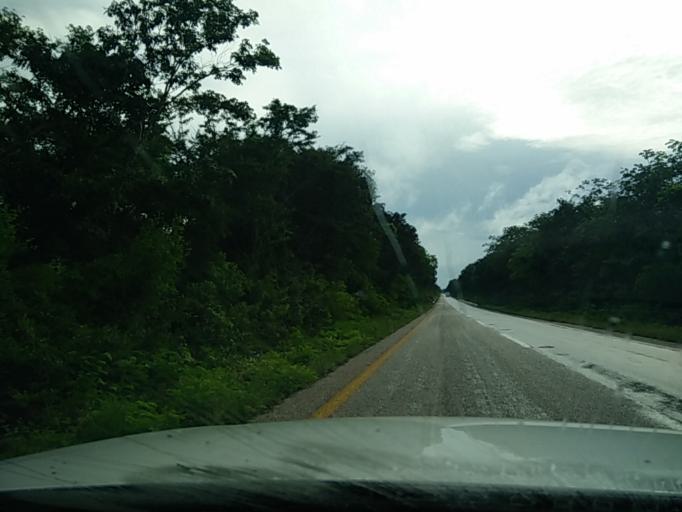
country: MX
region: Yucatan
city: Tunkas
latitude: 20.7540
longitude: -88.7393
